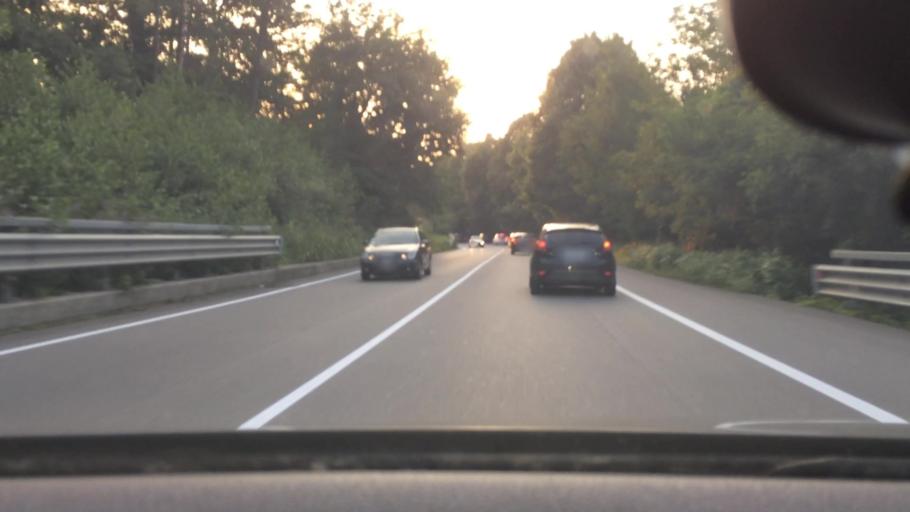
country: IT
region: Lombardy
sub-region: Provincia di Lecco
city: Cologna-Caraverio
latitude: 45.7484
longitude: 9.3376
